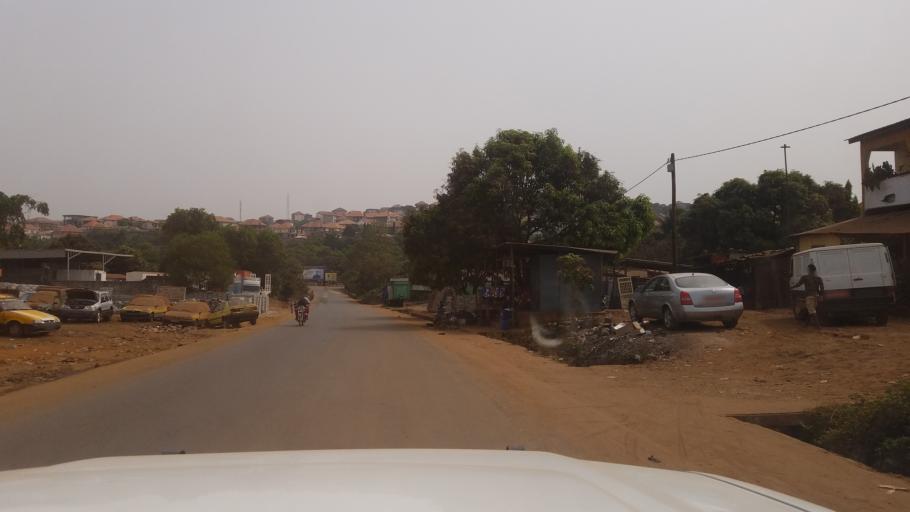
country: GN
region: Conakry
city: Conakry
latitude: 9.6464
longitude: -13.6045
